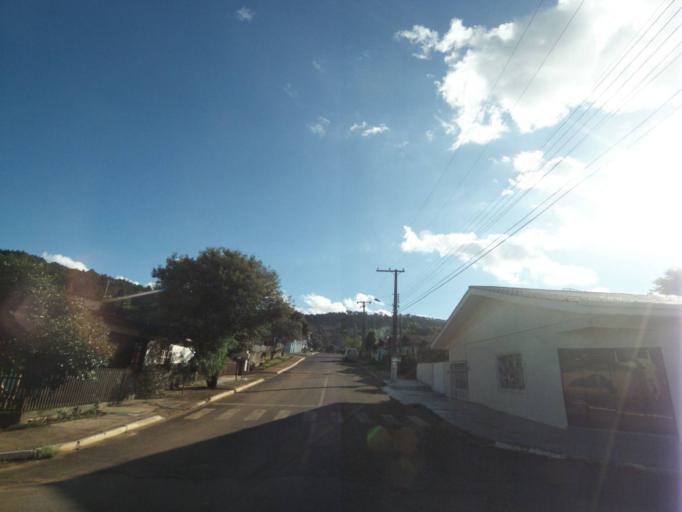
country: BR
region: Parana
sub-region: Uniao Da Vitoria
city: Uniao da Vitoria
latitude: -26.1667
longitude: -51.5352
